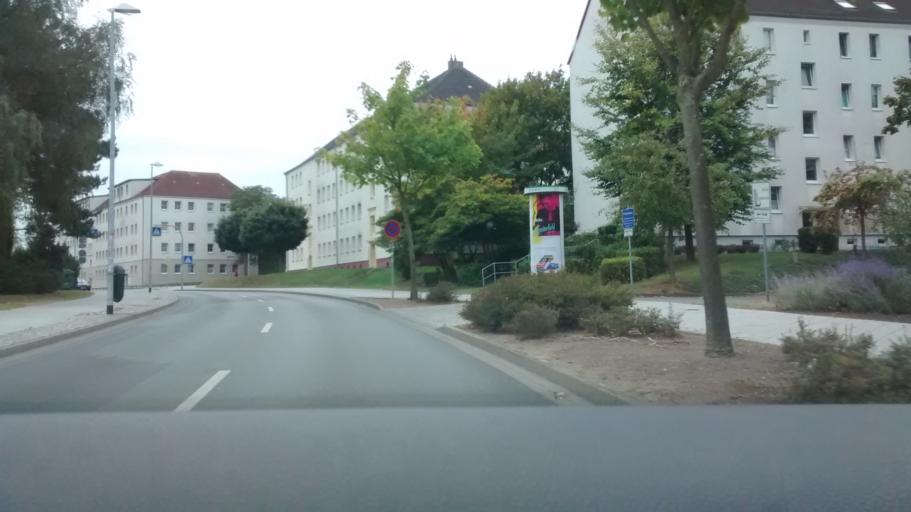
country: DE
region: Mecklenburg-Vorpommern
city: Wismar
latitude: 53.9035
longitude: 11.4206
